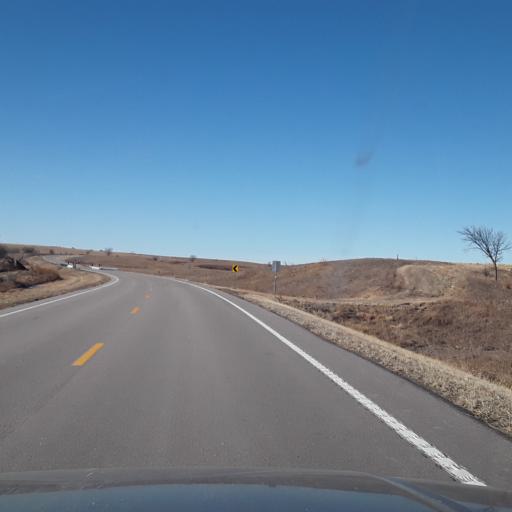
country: US
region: Nebraska
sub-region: Dawson County
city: Cozad
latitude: 40.6791
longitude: -100.1214
